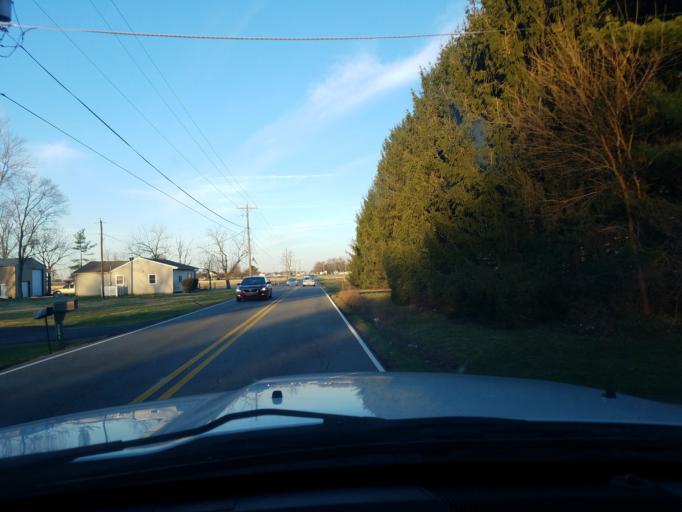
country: US
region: Indiana
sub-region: Johnson County
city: Whiteland
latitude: 39.5507
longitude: -86.0533
